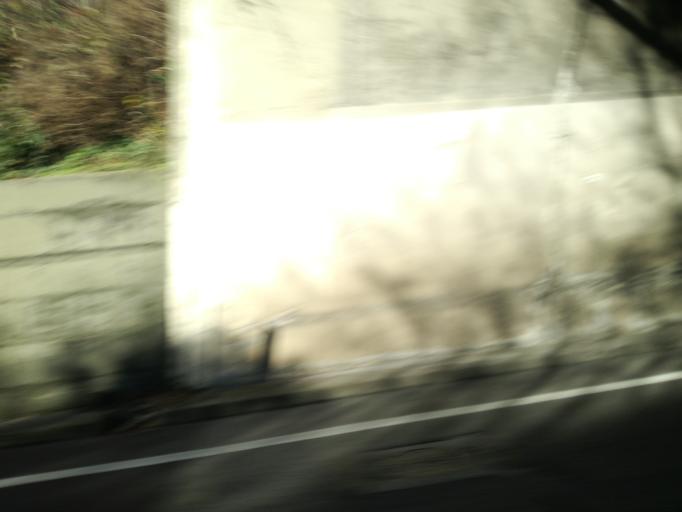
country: IT
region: Lombardy
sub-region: Provincia di Bergamo
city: Pianico
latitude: 45.8066
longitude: 10.0505
